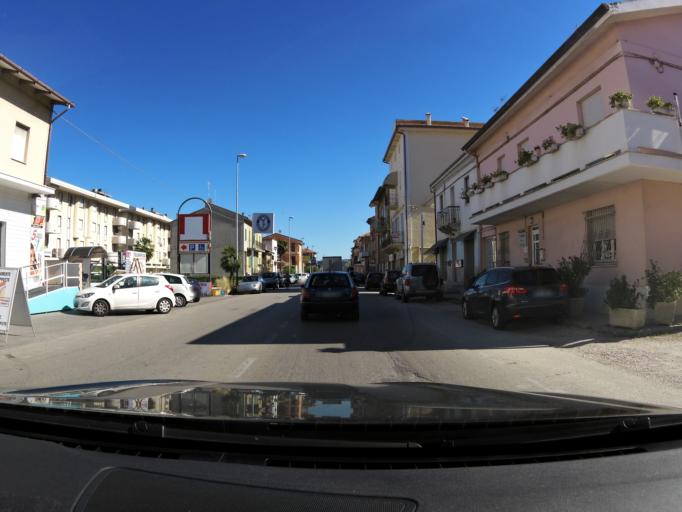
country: IT
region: The Marches
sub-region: Province of Fermo
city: Porto San Giorgio
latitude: 43.1736
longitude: 13.7965
